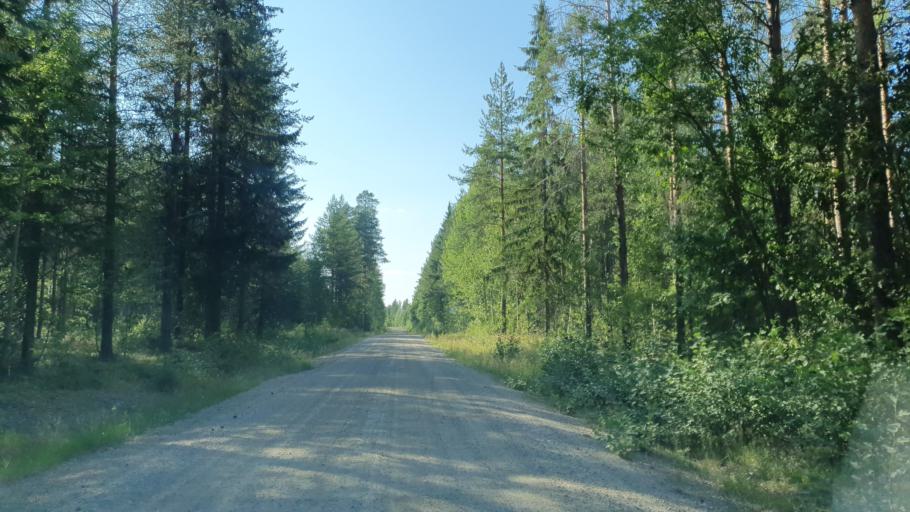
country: FI
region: Kainuu
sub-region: Kehys-Kainuu
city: Kuhmo
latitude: 64.0250
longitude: 29.7209
